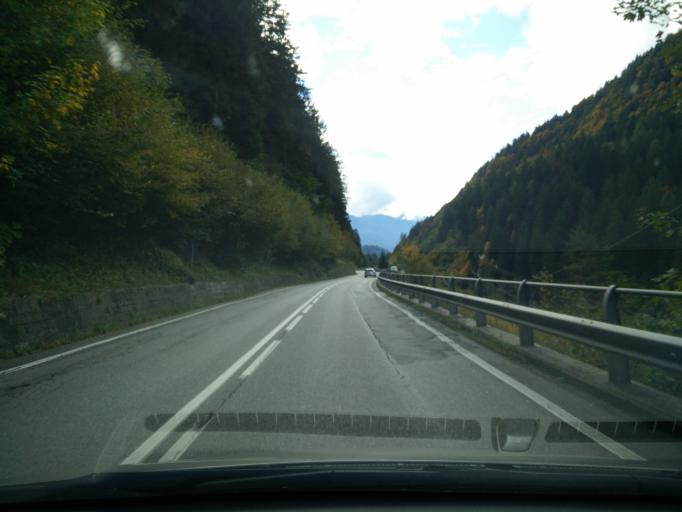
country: IT
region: Veneto
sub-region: Provincia di Belluno
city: Vigo di Cadore
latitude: 46.5295
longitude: 12.4686
